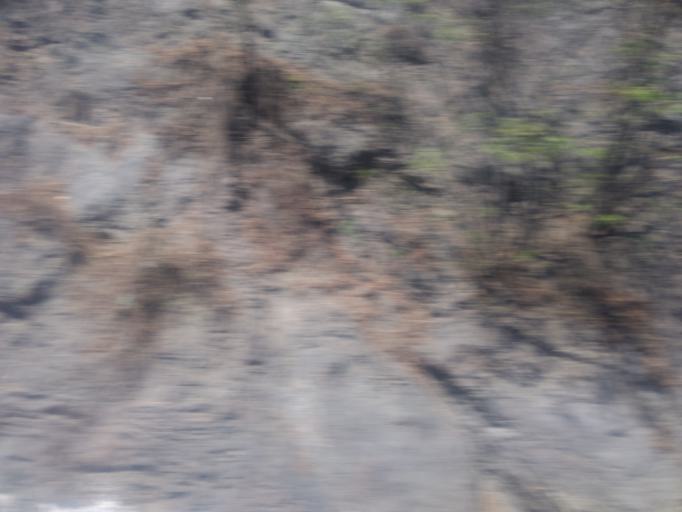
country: MX
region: Colima
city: El Colomo
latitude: 19.0556
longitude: -104.2690
